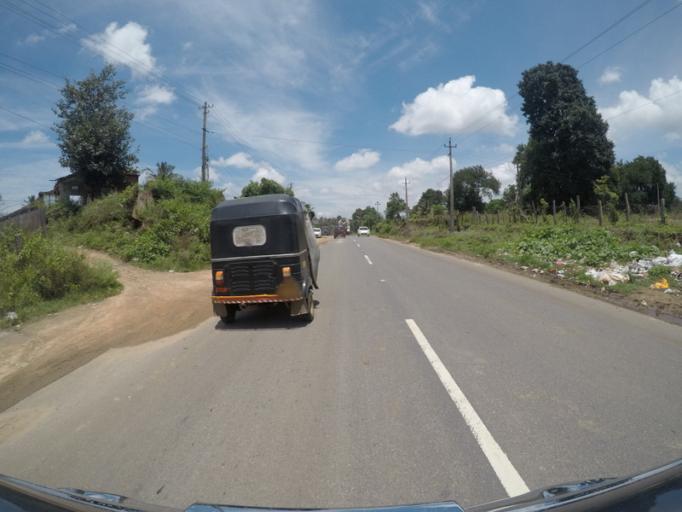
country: IN
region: Karnataka
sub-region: Kodagu
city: Kushalnagar
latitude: 12.4526
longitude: 75.9472
